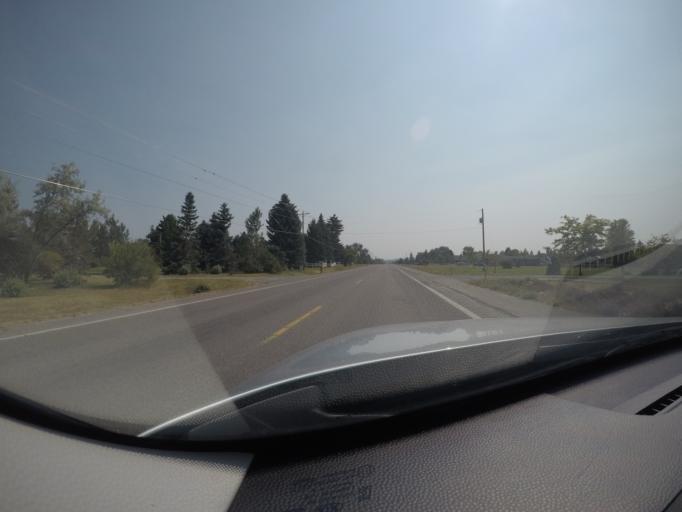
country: US
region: Montana
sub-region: Lake County
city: Polson
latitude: 47.7266
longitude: -114.1887
